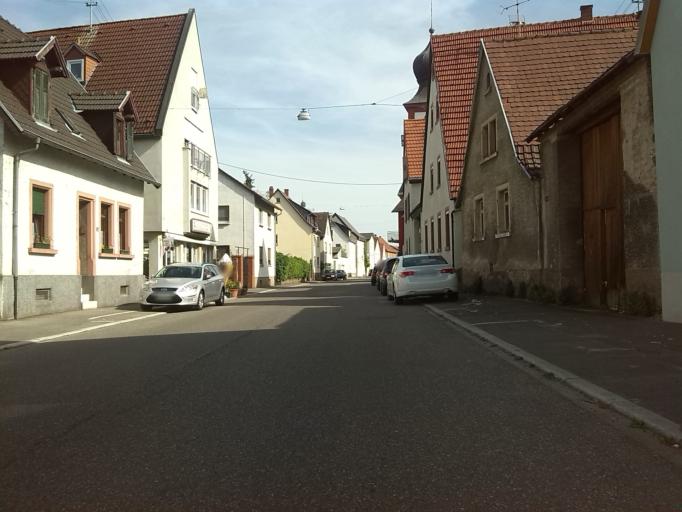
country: DE
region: Baden-Wuerttemberg
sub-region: Karlsruhe Region
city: Edingen-Neckarhausen
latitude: 49.4629
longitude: 8.6036
